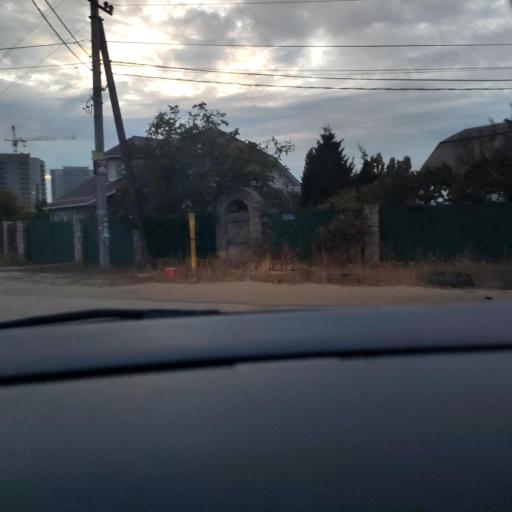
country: RU
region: Voronezj
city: Podgornoye
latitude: 51.7236
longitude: 39.1475
